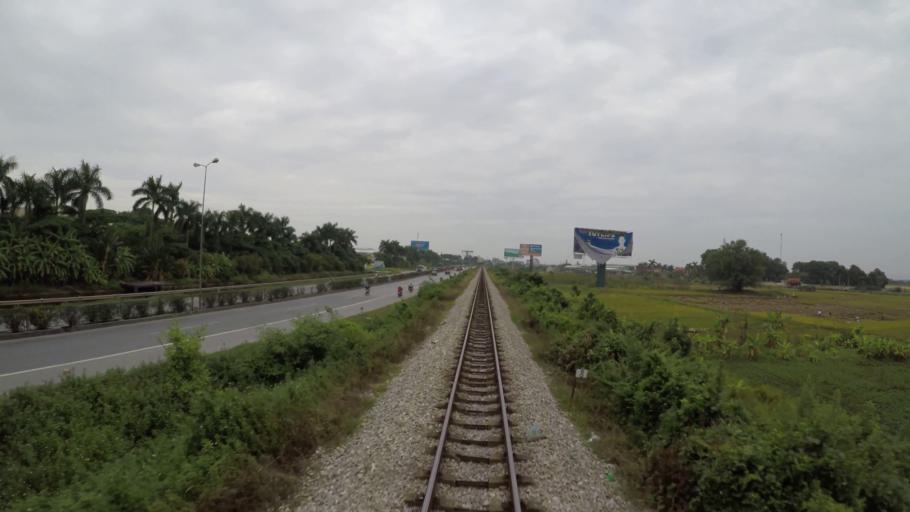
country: VN
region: Hai Duong
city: Thanh Pho Hai Duong
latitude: 20.9610
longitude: 106.3711
